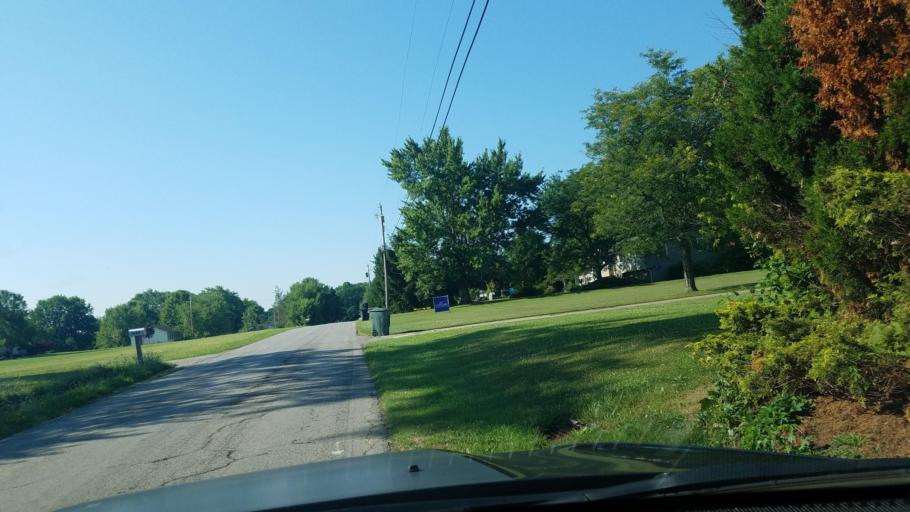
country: US
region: Ohio
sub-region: Trumbull County
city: Champion Heights
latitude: 41.2953
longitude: -80.8206
